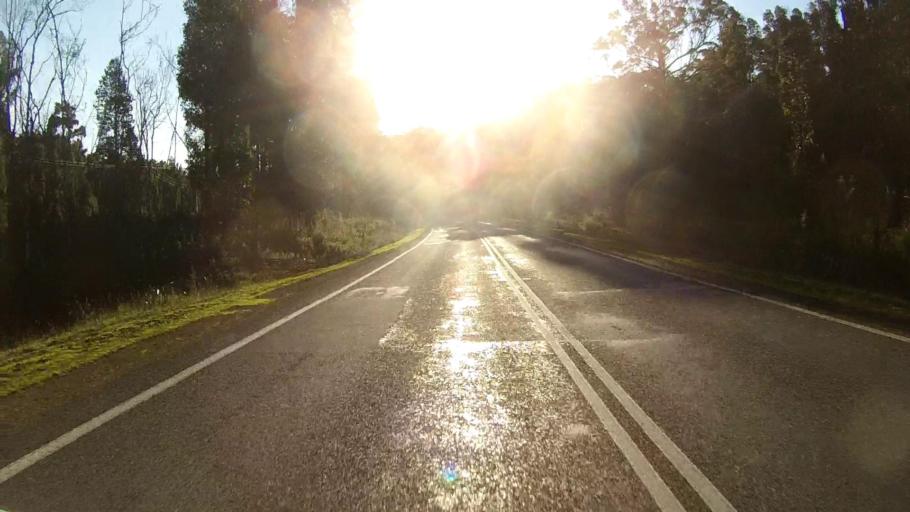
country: AU
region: Tasmania
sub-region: Sorell
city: Sorell
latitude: -42.9859
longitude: 147.9169
